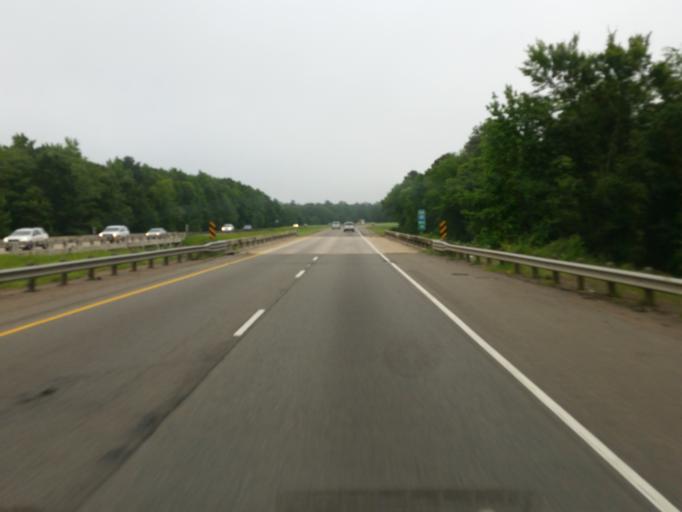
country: US
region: Louisiana
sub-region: Bossier Parish
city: Haughton
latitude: 32.5709
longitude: -93.4860
